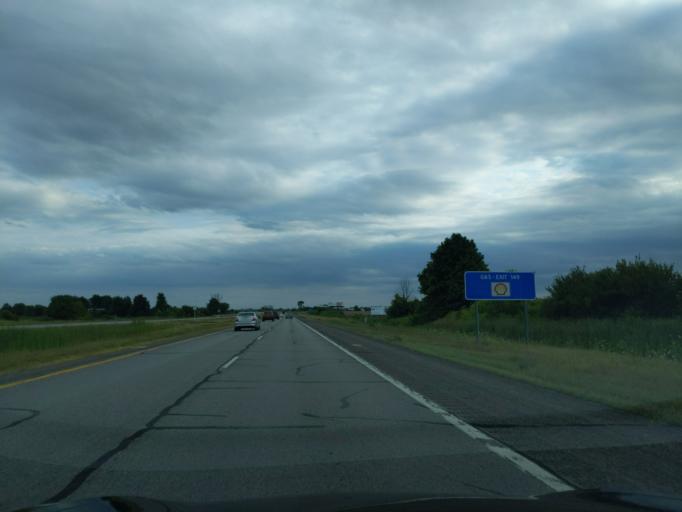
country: US
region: Michigan
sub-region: Clare County
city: Clare
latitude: 43.7094
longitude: -84.7577
